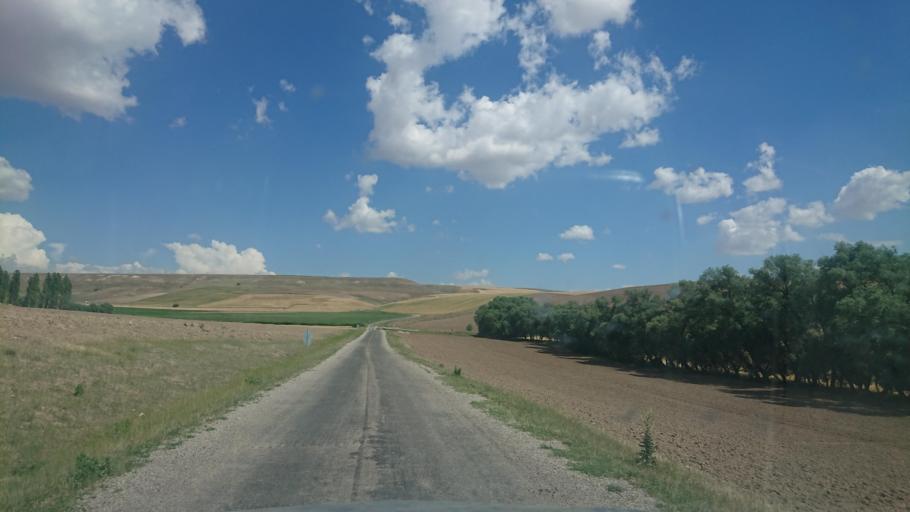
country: TR
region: Aksaray
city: Agacoren
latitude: 38.8164
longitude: 33.7944
